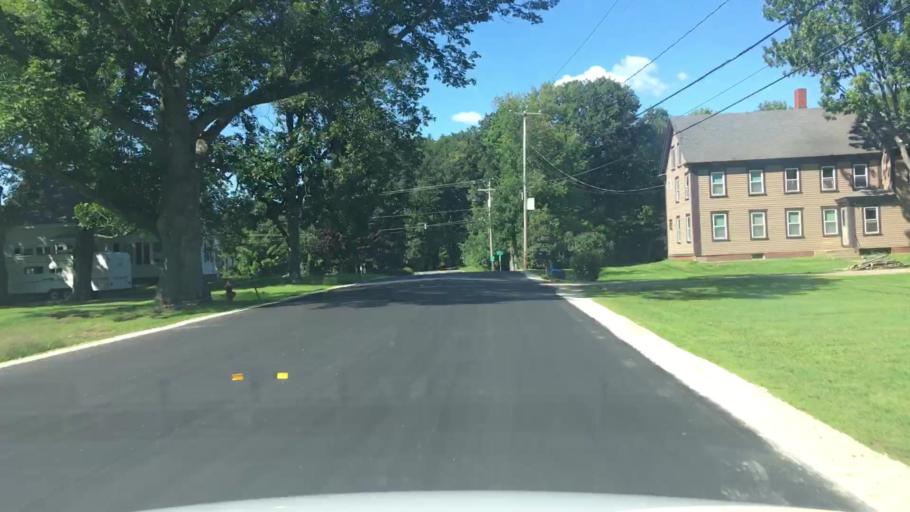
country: US
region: New Hampshire
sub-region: Strafford County
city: Dover
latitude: 43.1737
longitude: -70.8398
